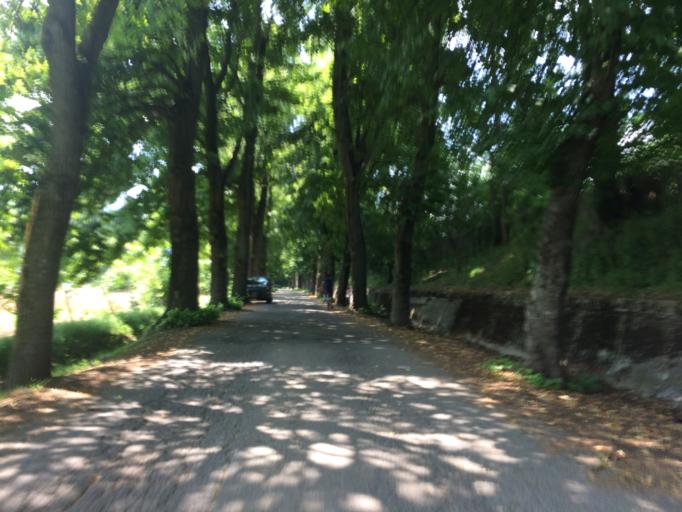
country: IT
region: Piedmont
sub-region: Provincia di Cuneo
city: Bagnasco
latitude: 44.3059
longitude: 8.0479
